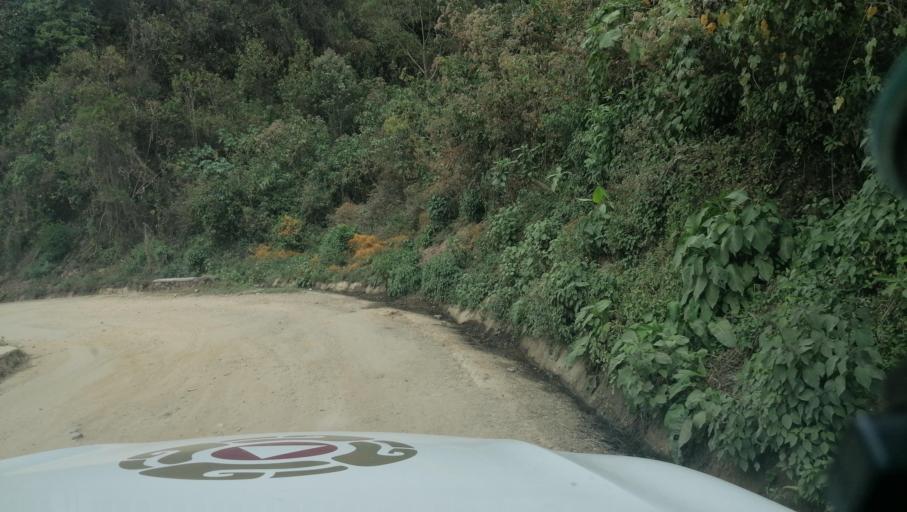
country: GT
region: San Marcos
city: Tacana
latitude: 15.2093
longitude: -92.1940
